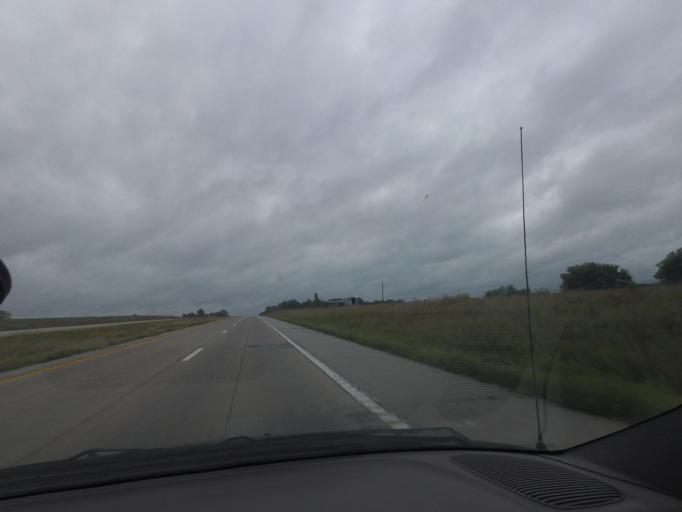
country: US
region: Missouri
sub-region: Marion County
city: Monroe City
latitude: 39.6736
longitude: -91.8837
